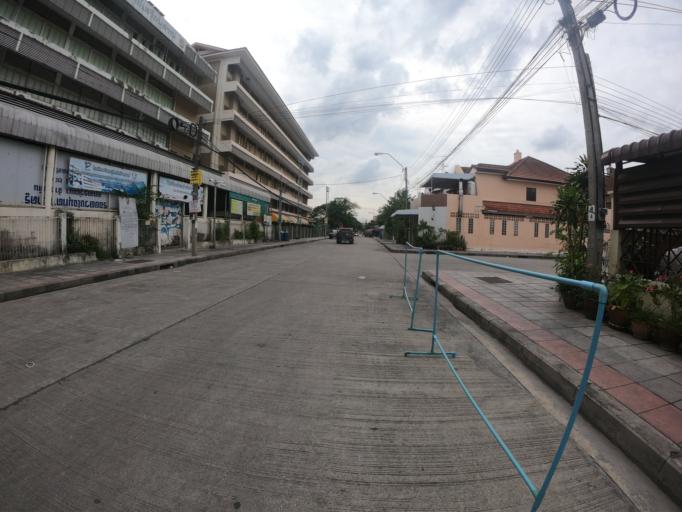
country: TH
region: Bangkok
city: Suan Luang
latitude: 13.7096
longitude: 100.6627
